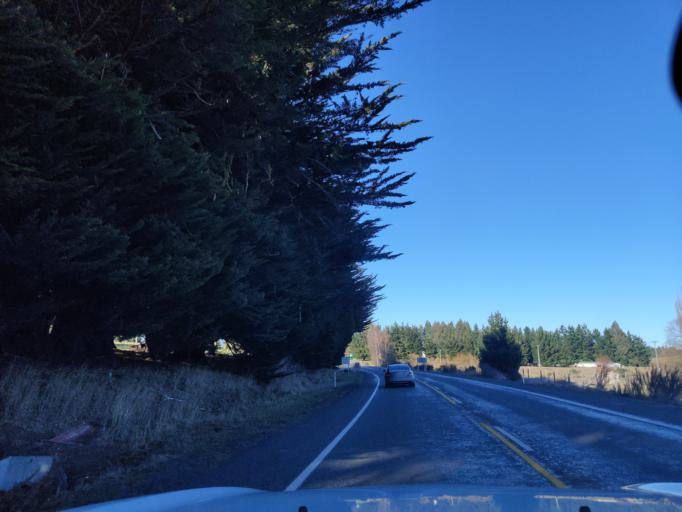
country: NZ
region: Manawatu-Wanganui
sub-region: Ruapehu District
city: Waiouru
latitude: -39.4726
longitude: 175.6689
